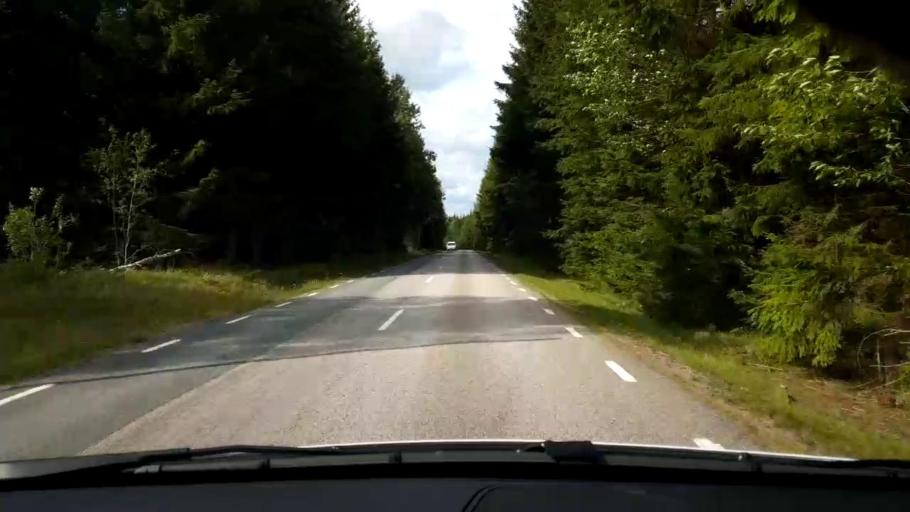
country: SE
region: Joenkoeping
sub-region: Vetlanda Kommun
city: Vetlanda
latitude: 57.3532
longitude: 15.0728
